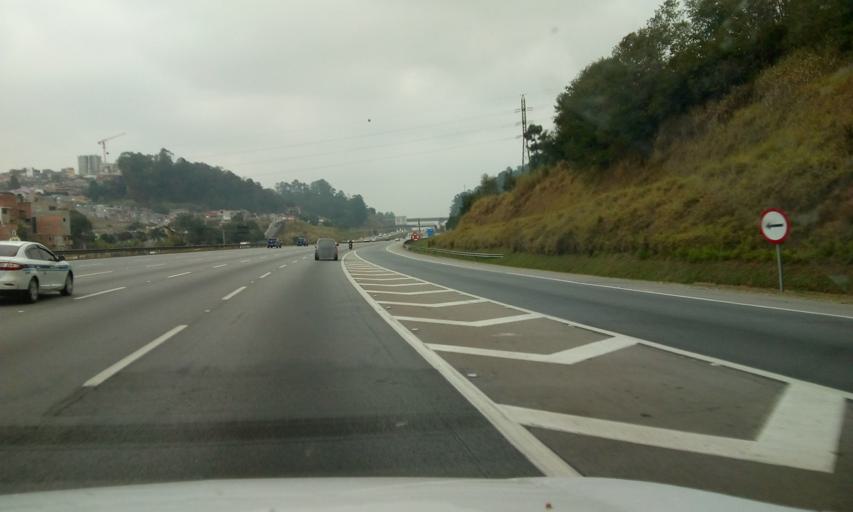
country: BR
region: Sao Paulo
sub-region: Caieiras
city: Caieiras
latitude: -23.4414
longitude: -46.7571
